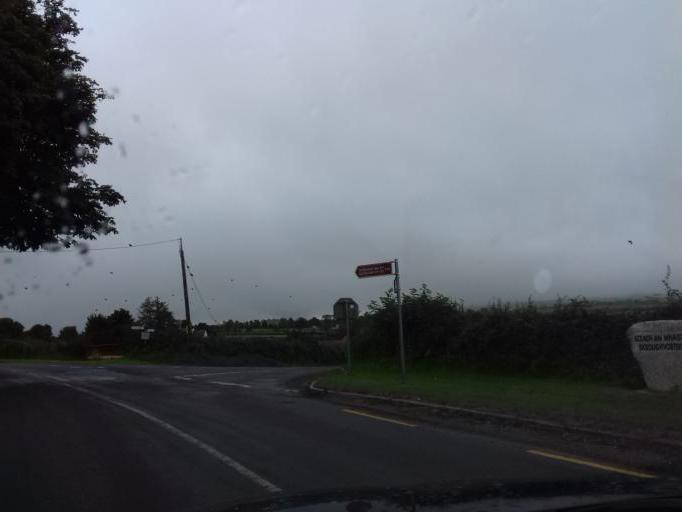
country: IE
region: Leinster
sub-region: Kilkenny
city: Graiguenamanagh
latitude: 52.5996
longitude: -6.9927
